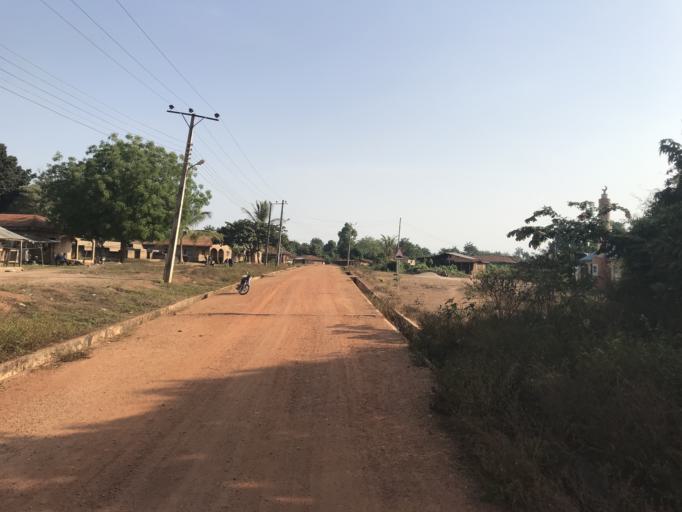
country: NG
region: Osun
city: Bode Osi
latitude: 7.7695
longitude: 4.3050
